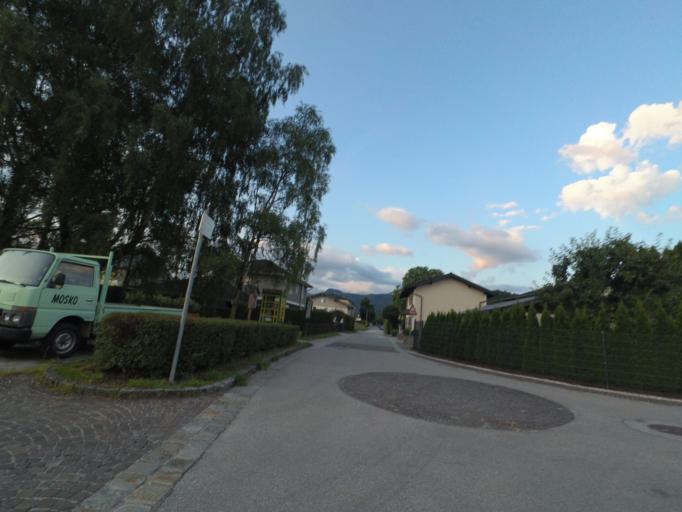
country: AT
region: Salzburg
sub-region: Politischer Bezirk Salzburg-Umgebung
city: Anif
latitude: 47.7371
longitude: 13.0548
